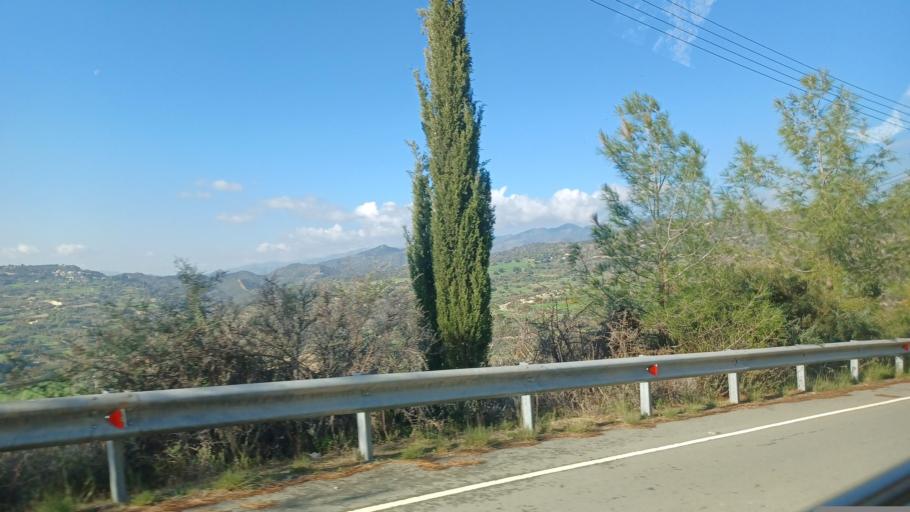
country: CY
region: Larnaka
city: Kofinou
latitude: 34.8442
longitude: 33.2968
